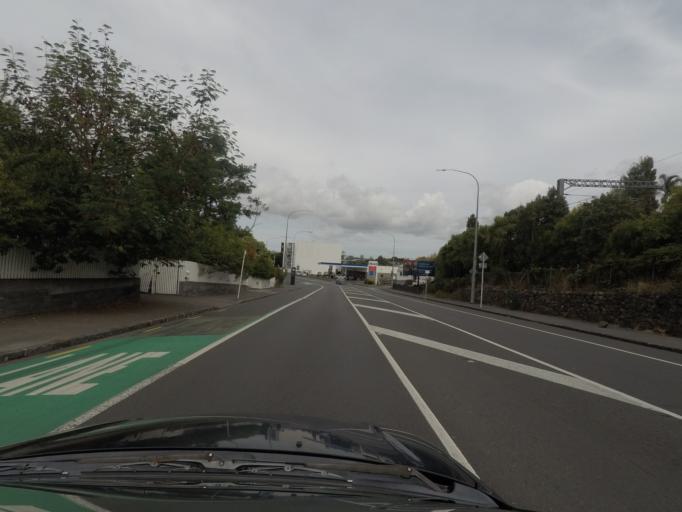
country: NZ
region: Auckland
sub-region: Auckland
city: Auckland
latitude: -36.8734
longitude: 174.7430
